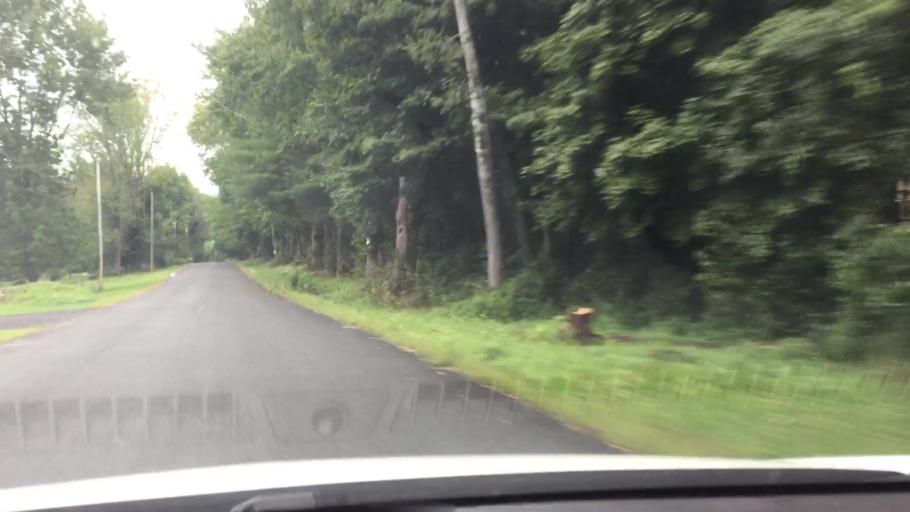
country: US
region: Massachusetts
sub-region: Berkshire County
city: Richmond
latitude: 42.3640
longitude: -73.3681
